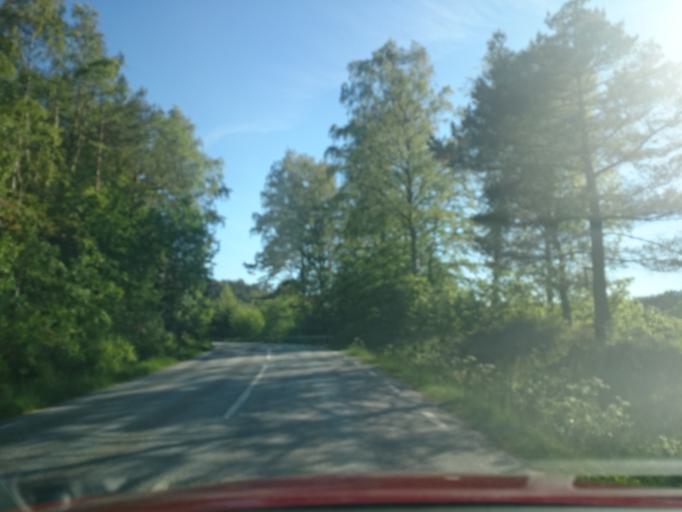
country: SE
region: Vaestra Goetaland
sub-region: Lysekils Kommun
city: Lysekil
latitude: 58.2768
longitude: 11.5319
